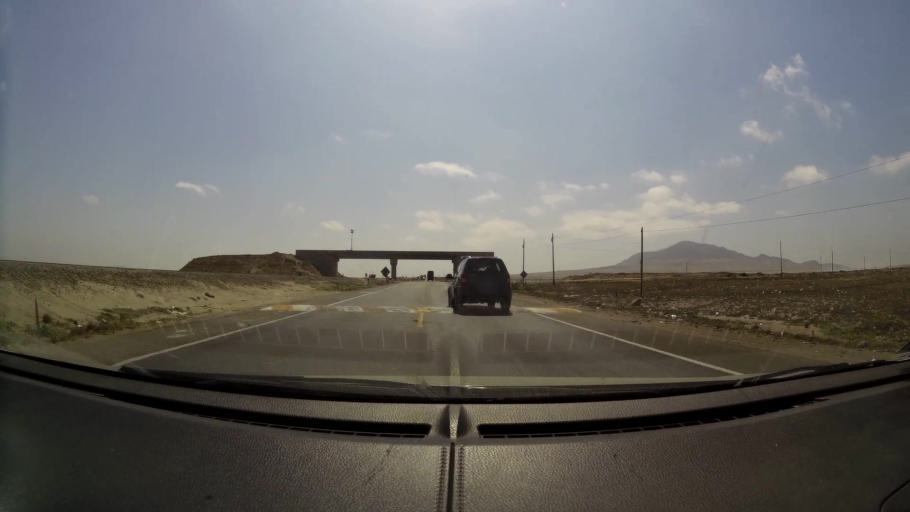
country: PE
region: Lambayeque
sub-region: Provincia de Chiclayo
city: Reque
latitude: -6.9272
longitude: -79.7421
